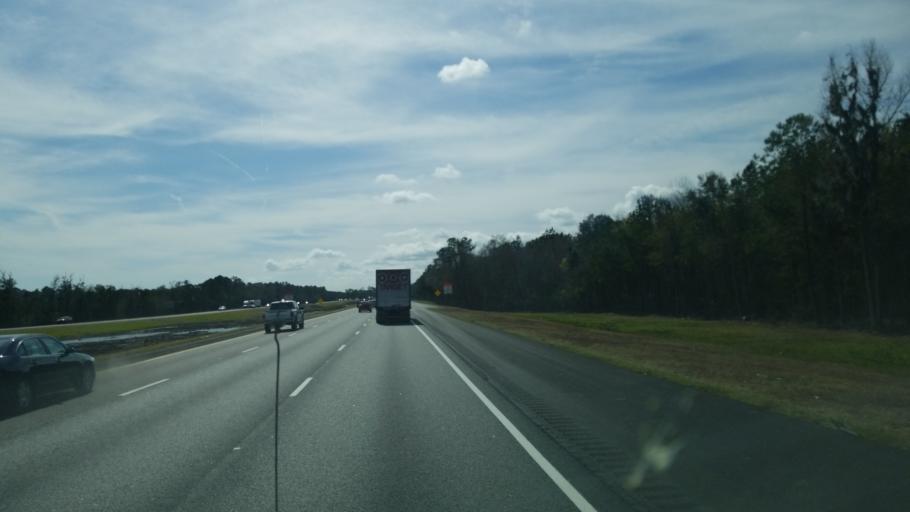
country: US
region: Georgia
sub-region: Liberty County
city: Midway
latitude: 31.7592
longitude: -81.3826
